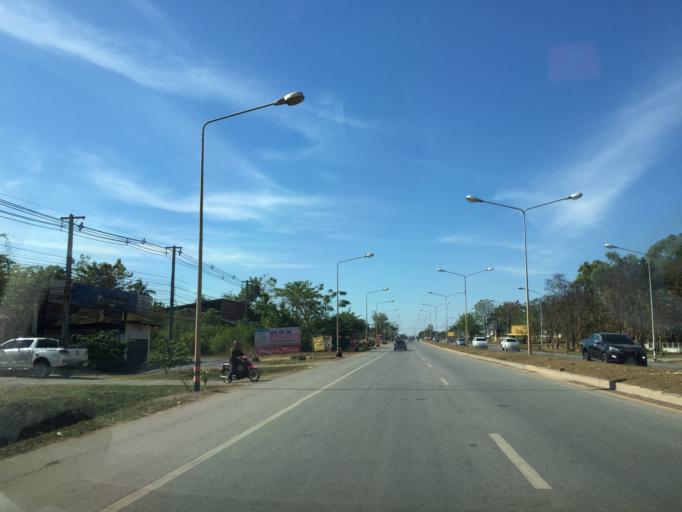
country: TH
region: Changwat Nong Bua Lamphu
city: Na Klang
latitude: 17.3051
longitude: 102.1907
